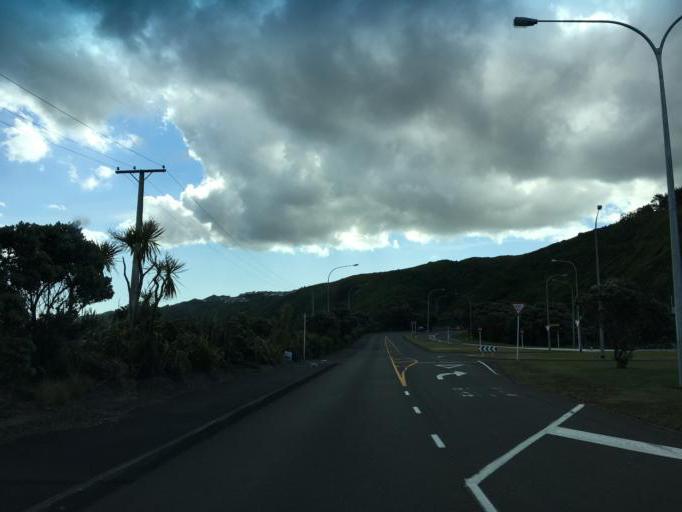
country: NZ
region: Wellington
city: Petone
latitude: -41.2249
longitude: 174.8630
